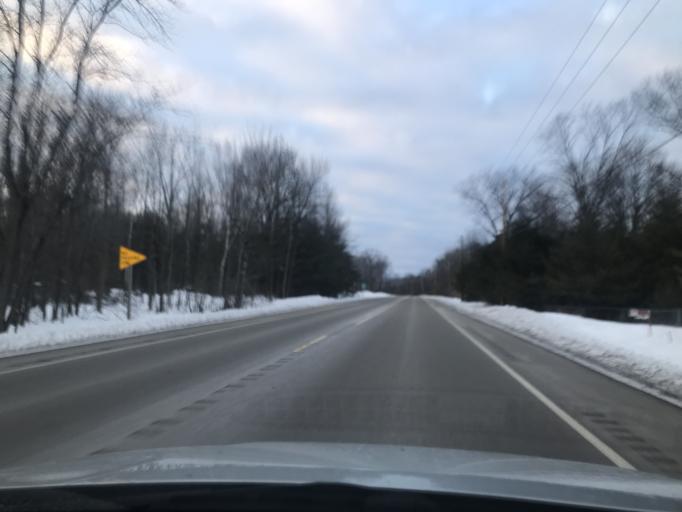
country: US
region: Wisconsin
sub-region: Marinette County
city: Marinette
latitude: 45.1506
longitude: -87.7043
